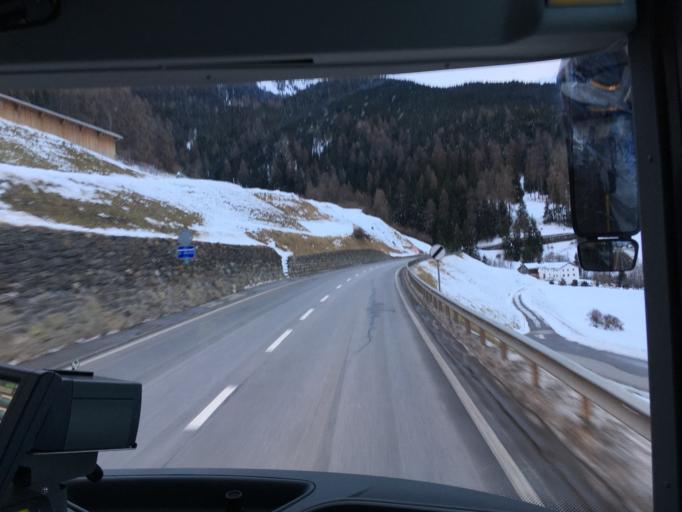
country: CH
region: Grisons
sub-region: Albula District
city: Tiefencastel
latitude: 46.5791
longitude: 9.6221
